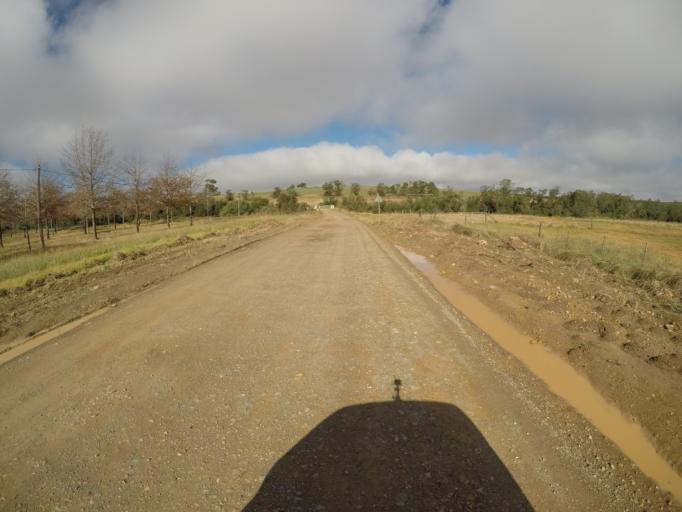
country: ZA
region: Western Cape
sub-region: Cape Winelands District Municipality
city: Ashton
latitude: -34.1272
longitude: 19.8399
